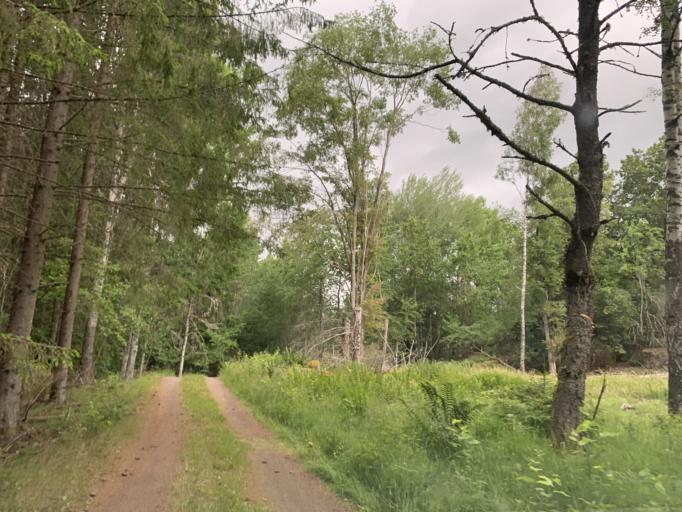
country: SE
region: Kalmar
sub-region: Vasterviks Kommun
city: Overum
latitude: 58.0271
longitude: 16.1176
